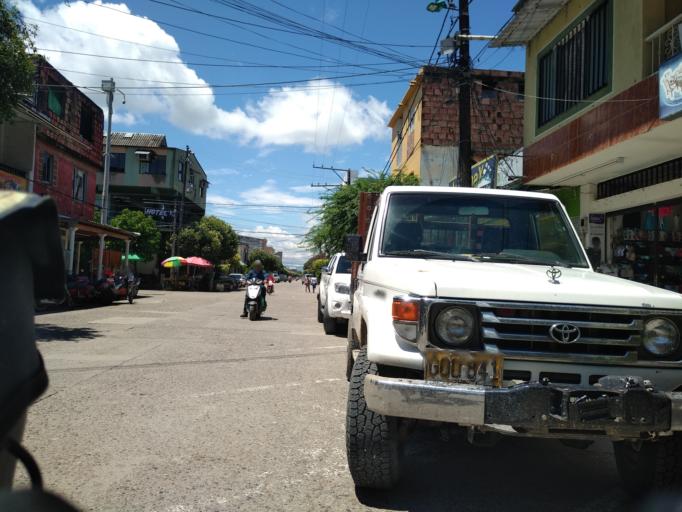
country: CO
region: Boyaca
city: Puerto Boyaca
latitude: 5.9766
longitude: -74.5911
